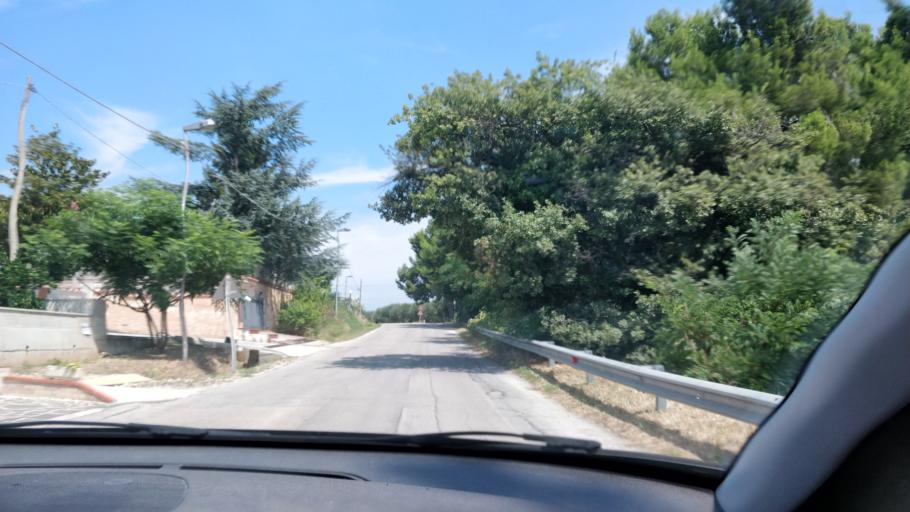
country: IT
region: Abruzzo
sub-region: Provincia di Chieti
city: Torrevecchia
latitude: 42.3941
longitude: 14.1994
